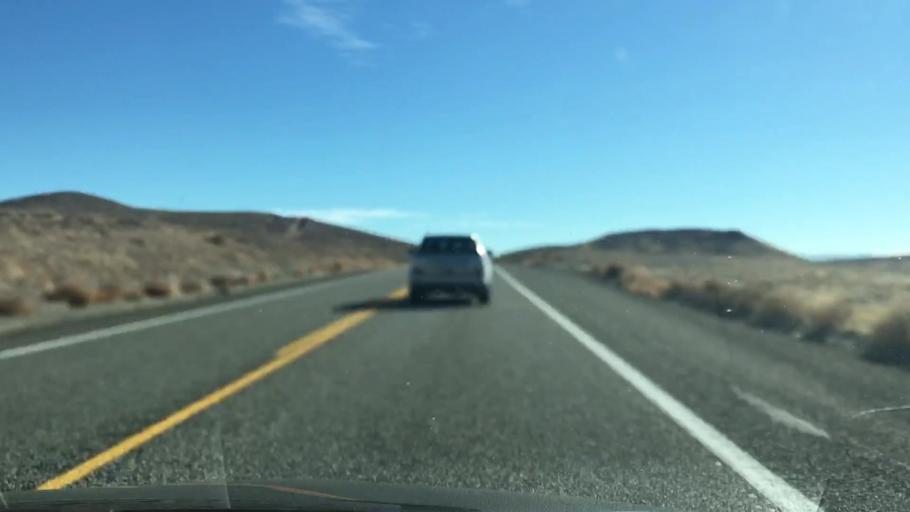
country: US
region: Nevada
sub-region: Lyon County
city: Silver Springs
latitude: 39.2308
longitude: -119.2301
